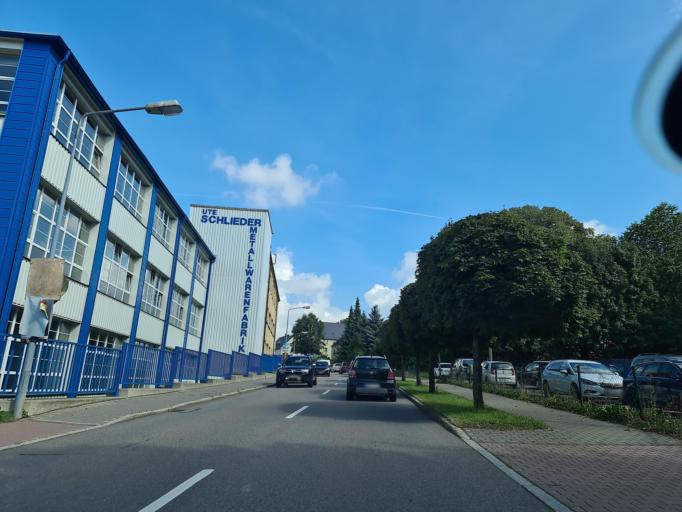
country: DE
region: Saxony
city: Zoblitz
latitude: 50.6583
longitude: 13.2254
